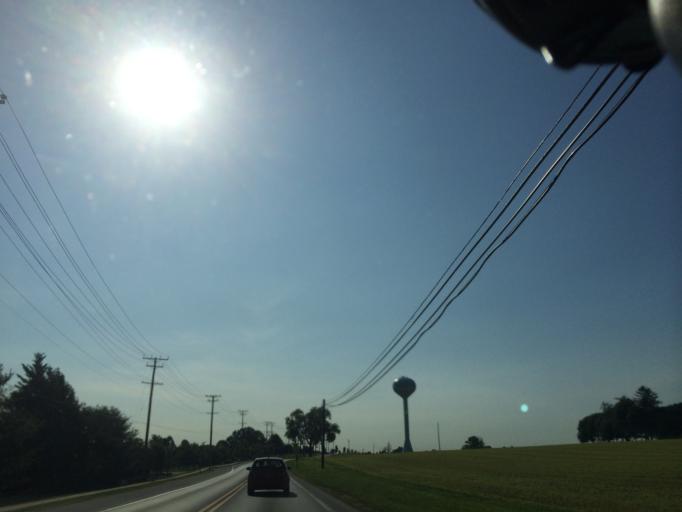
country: US
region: Maryland
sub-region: Howard County
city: Fulton
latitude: 39.1503
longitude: -76.9178
